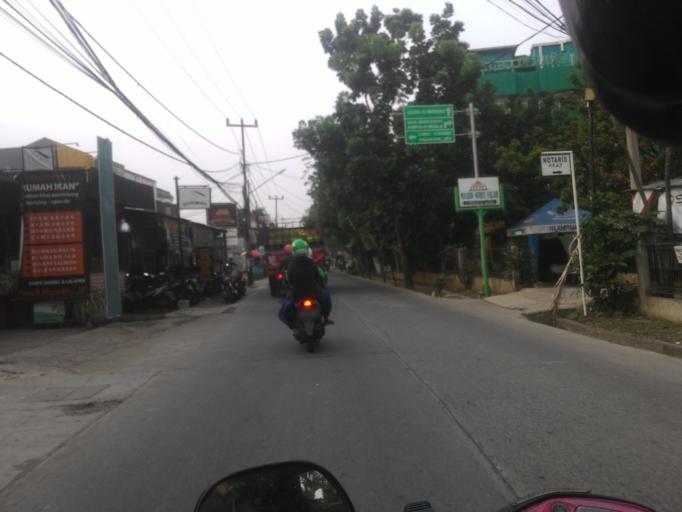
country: ID
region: West Java
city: Depok
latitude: -6.3716
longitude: 106.8132
